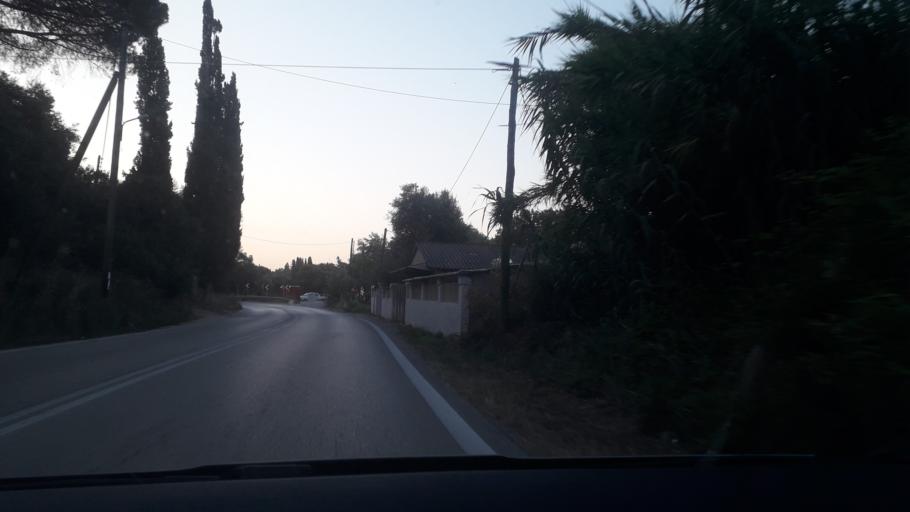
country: GR
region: Ionian Islands
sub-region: Nomos Kerkyras
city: Agios Matthaios
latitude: 39.4771
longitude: 19.9235
